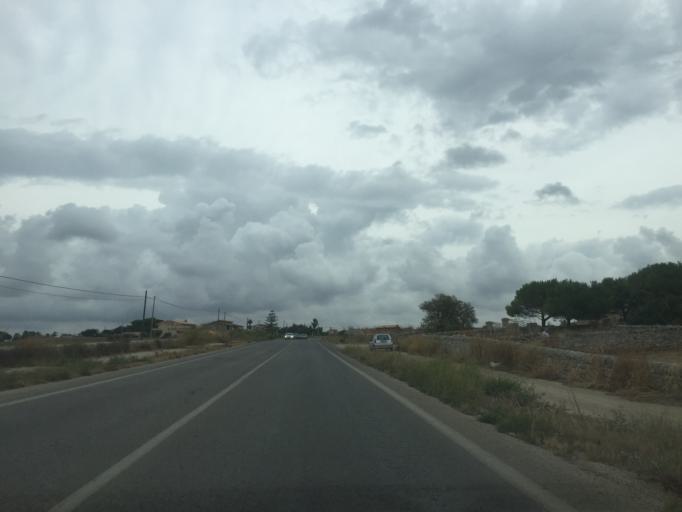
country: IT
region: Sicily
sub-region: Ragusa
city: Marina di Ragusa
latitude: 36.8088
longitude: 14.5649
